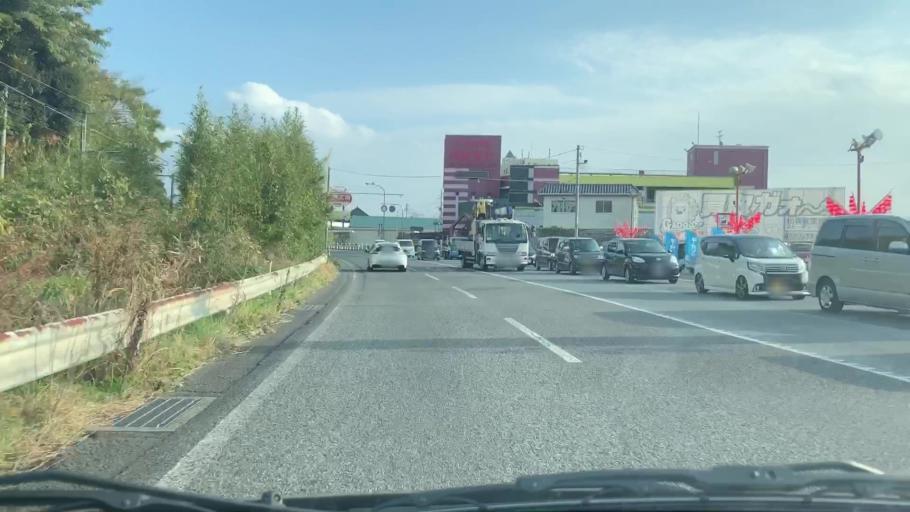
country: JP
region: Nagasaki
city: Sasebo
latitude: 33.1436
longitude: 129.7867
